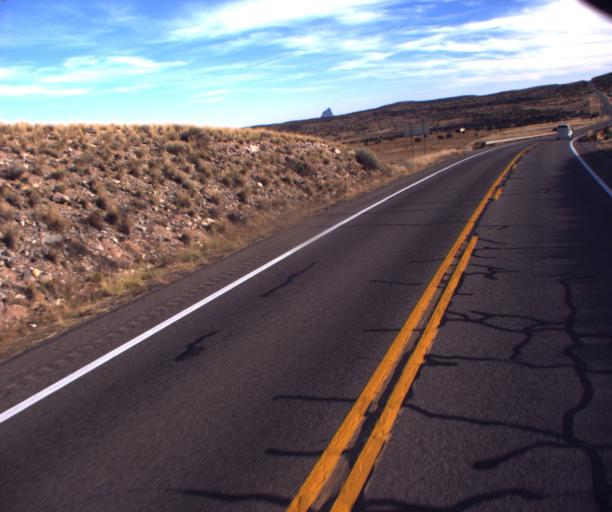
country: US
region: New Mexico
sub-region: San Juan County
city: Shiprock
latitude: 36.8779
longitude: -109.0475
